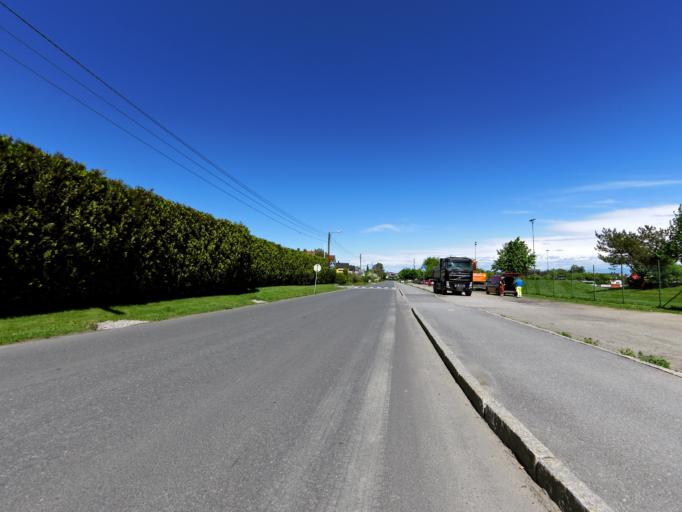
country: NO
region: Ostfold
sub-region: Fredrikstad
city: Fredrikstad
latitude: 59.2300
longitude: 10.9705
